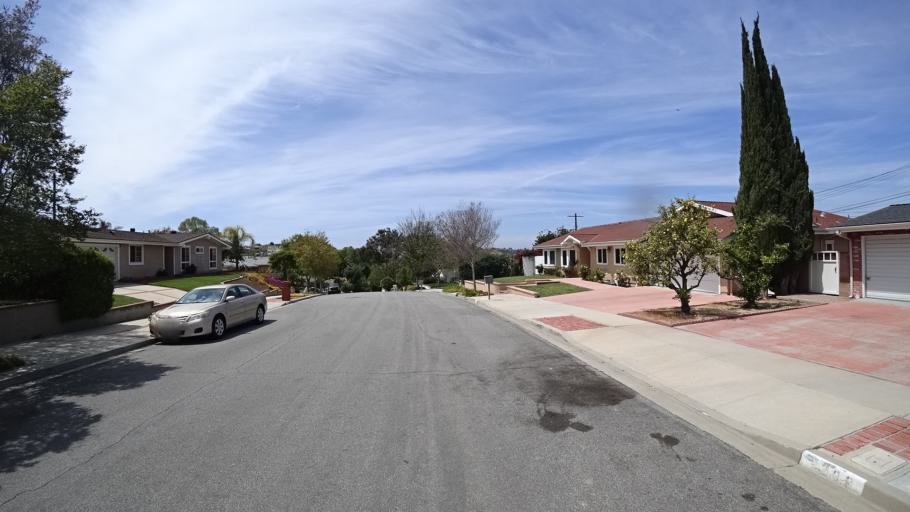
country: US
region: California
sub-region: Ventura County
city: Thousand Oaks
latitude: 34.1914
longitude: -118.8720
